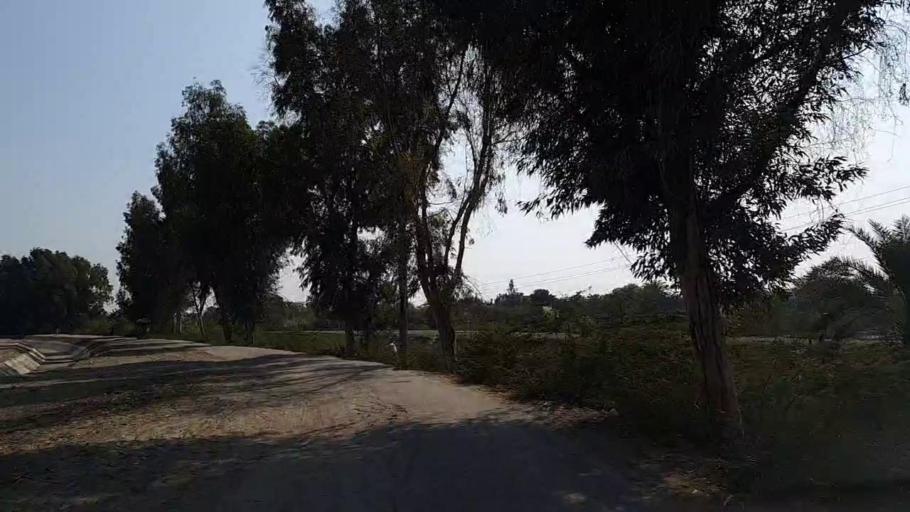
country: PK
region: Sindh
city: Jam Sahib
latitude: 26.2746
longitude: 68.5559
